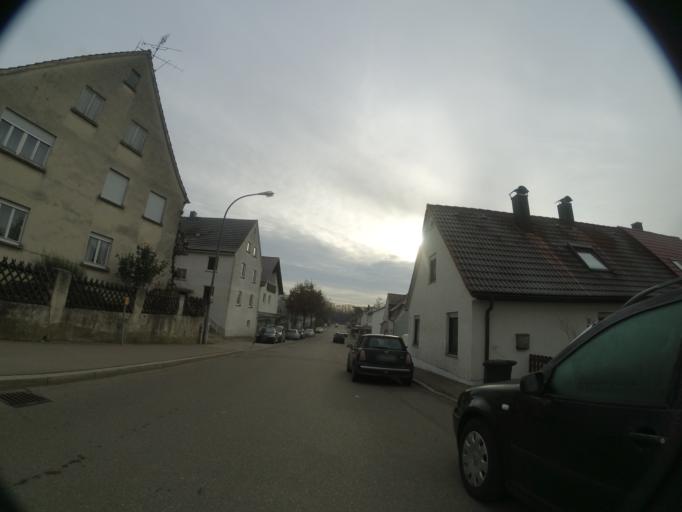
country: DE
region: Bavaria
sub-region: Swabia
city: Neu-Ulm
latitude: 48.4367
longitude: 10.0519
